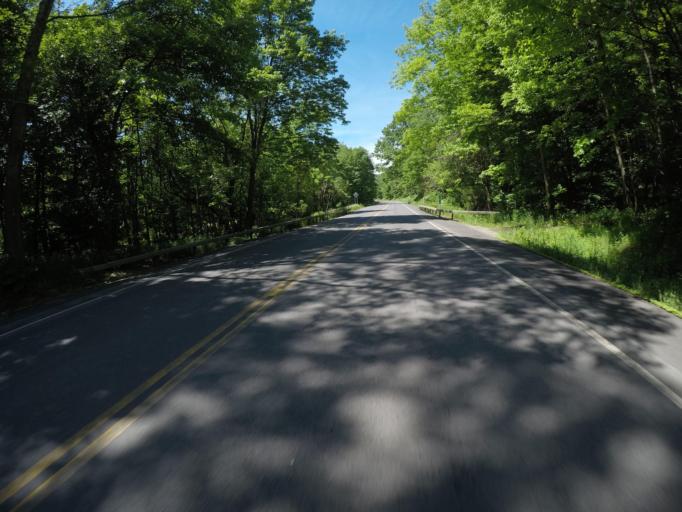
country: US
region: New York
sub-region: Delaware County
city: Delhi
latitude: 42.2634
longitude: -74.9286
